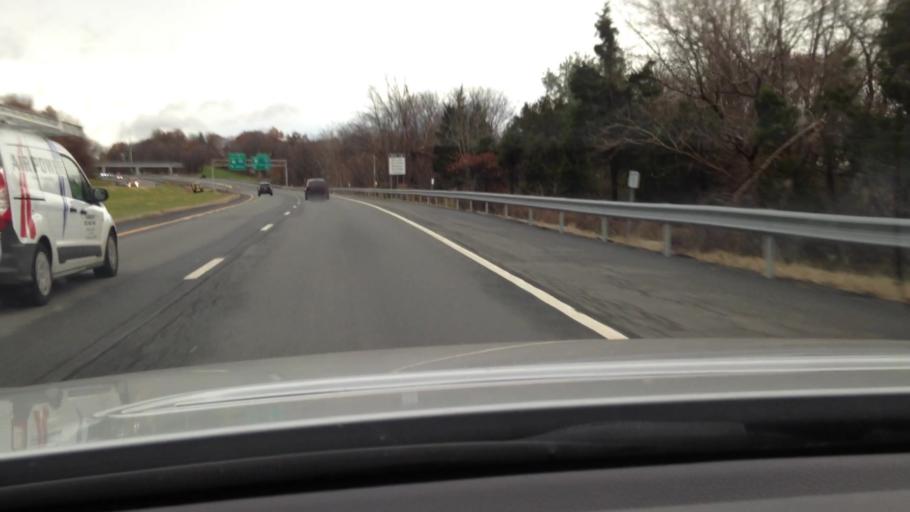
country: US
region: New York
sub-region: Rockland County
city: Chestnut Ridge
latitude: 41.0872
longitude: -74.0424
